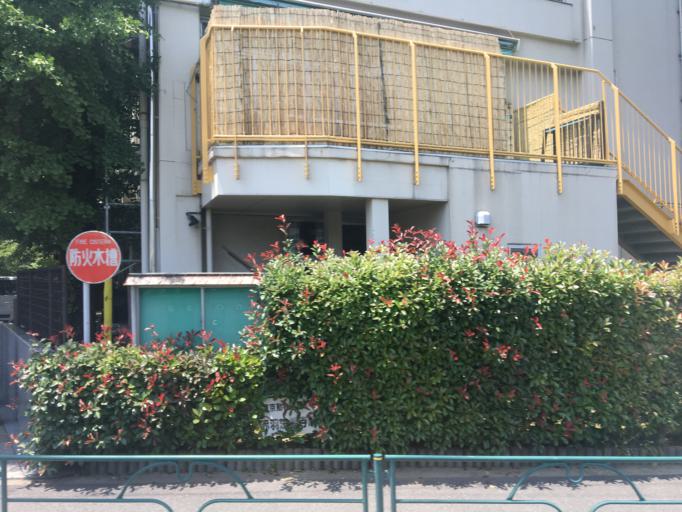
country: JP
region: Saitama
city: Kawaguchi
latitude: 35.7790
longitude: 139.7136
